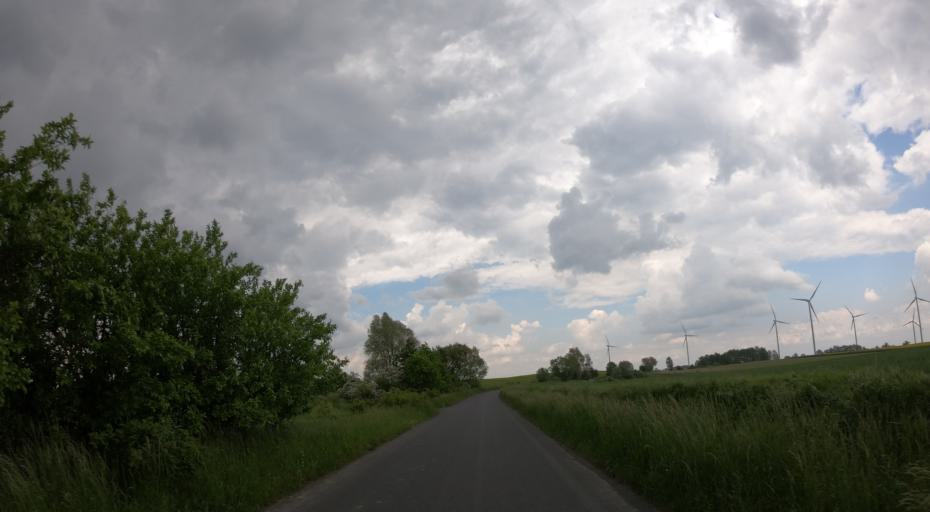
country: PL
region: West Pomeranian Voivodeship
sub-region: Powiat pyrzycki
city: Bielice
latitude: 53.1405
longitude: 14.7622
